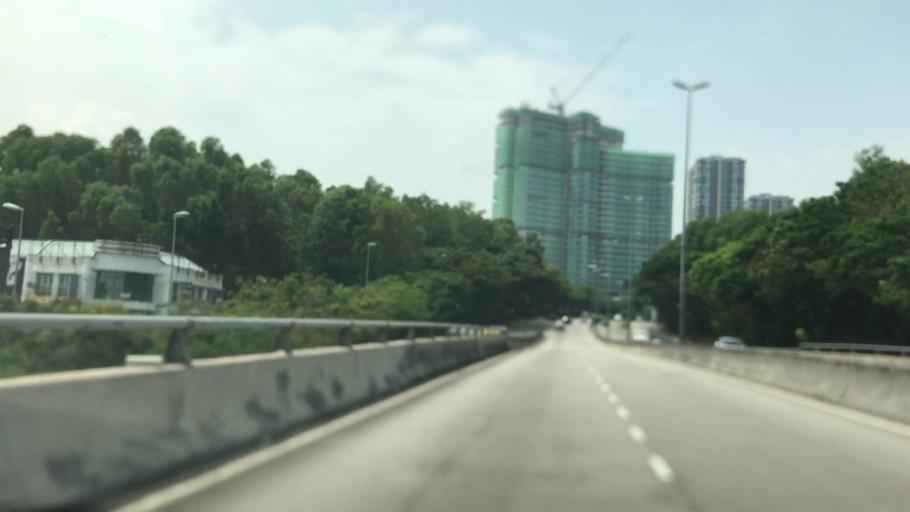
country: MY
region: Selangor
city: Subang Jaya
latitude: 3.0246
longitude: 101.6188
